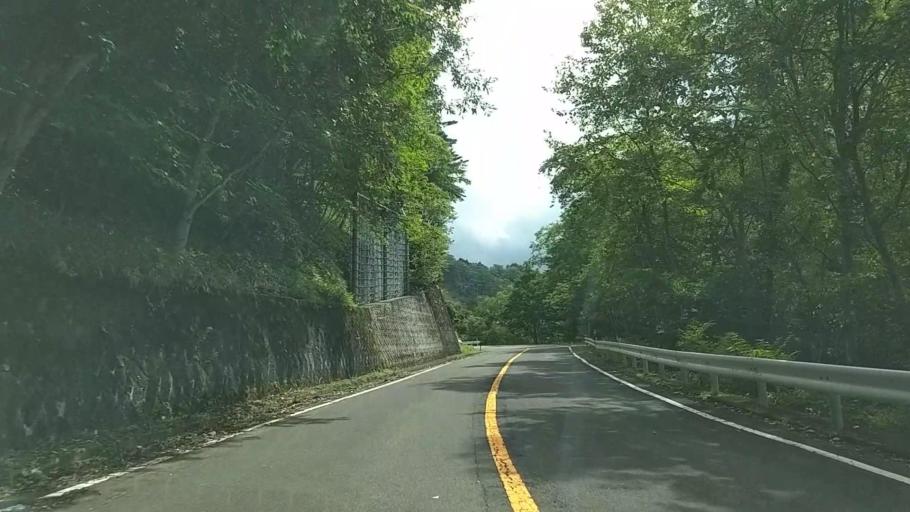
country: JP
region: Tochigi
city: Nikko
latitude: 36.7255
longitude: 139.4928
